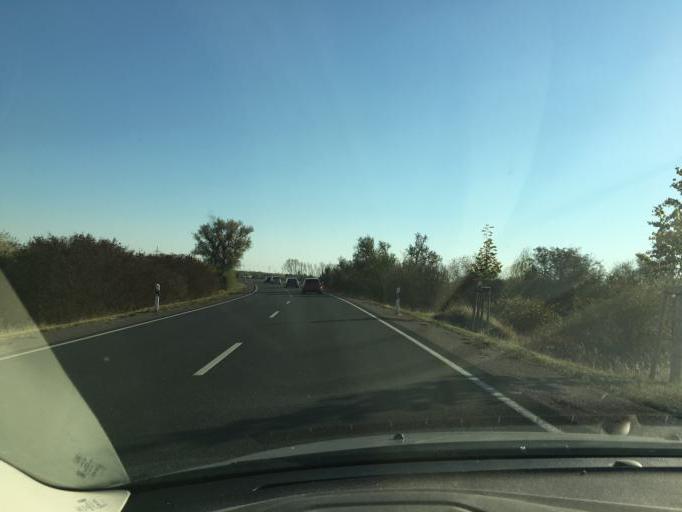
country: DE
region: Saxony-Anhalt
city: Roitzsch
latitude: 51.5886
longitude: 12.2785
